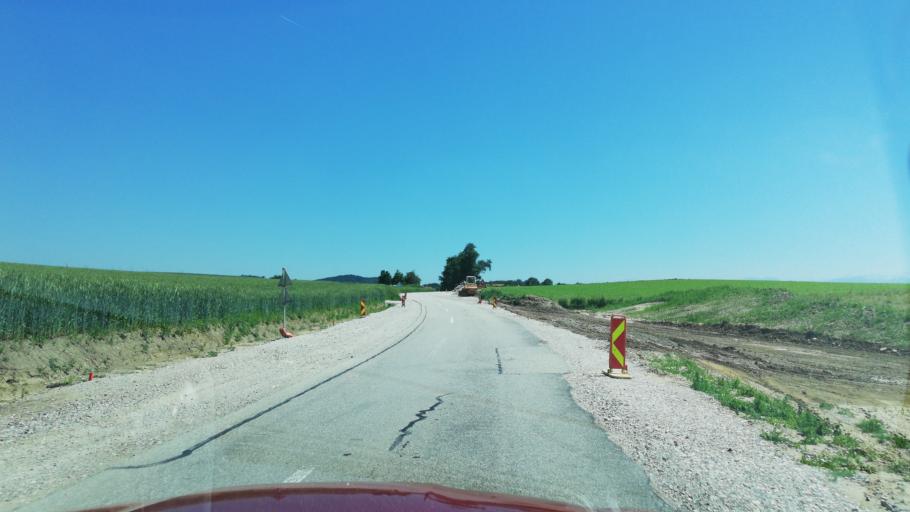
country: AT
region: Upper Austria
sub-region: Wels-Land
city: Bachmanning
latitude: 48.1300
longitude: 13.7714
